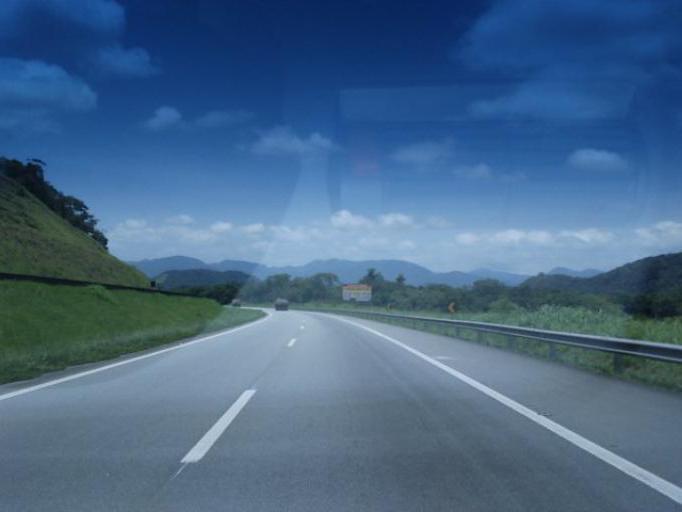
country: BR
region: Sao Paulo
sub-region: Miracatu
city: Miracatu
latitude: -24.2069
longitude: -47.3723
